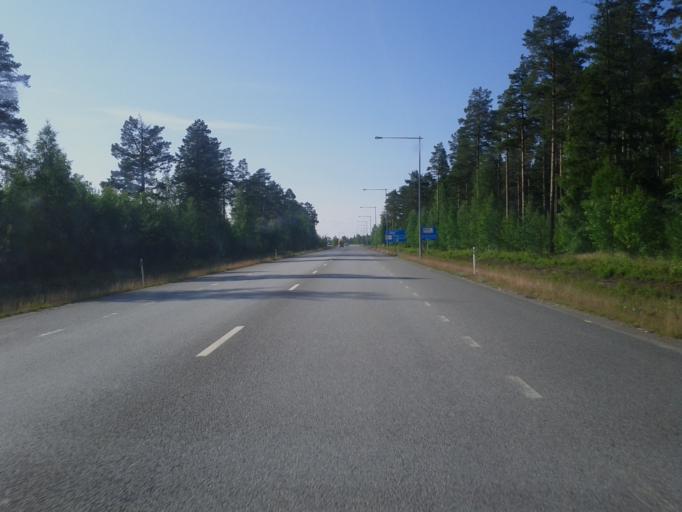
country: SE
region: Vaesterbotten
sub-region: Umea Kommun
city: Umea
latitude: 63.7942
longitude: 20.2934
